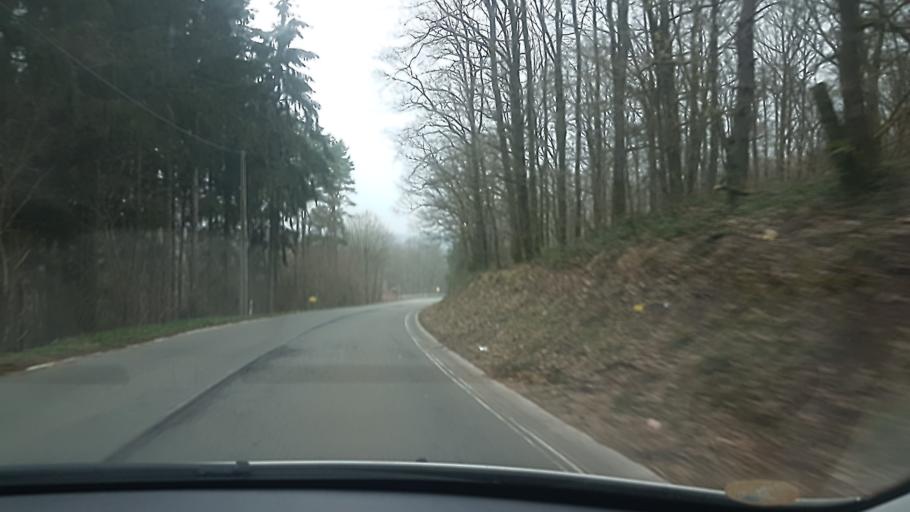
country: BE
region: Wallonia
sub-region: Province de Namur
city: Couvin
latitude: 50.0605
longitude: 4.6071
